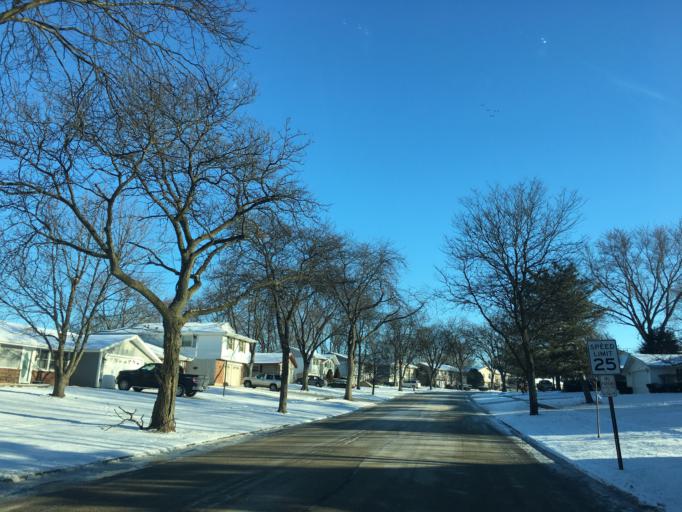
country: US
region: Illinois
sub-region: Cook County
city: Schaumburg
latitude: 42.0220
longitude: -88.1055
